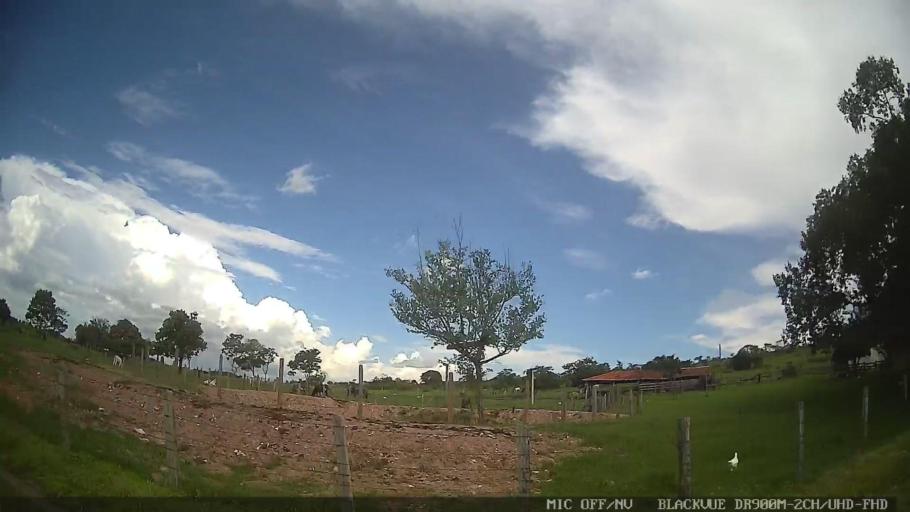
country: BR
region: Sao Paulo
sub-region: Conchas
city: Conchas
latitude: -22.9940
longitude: -47.9986
